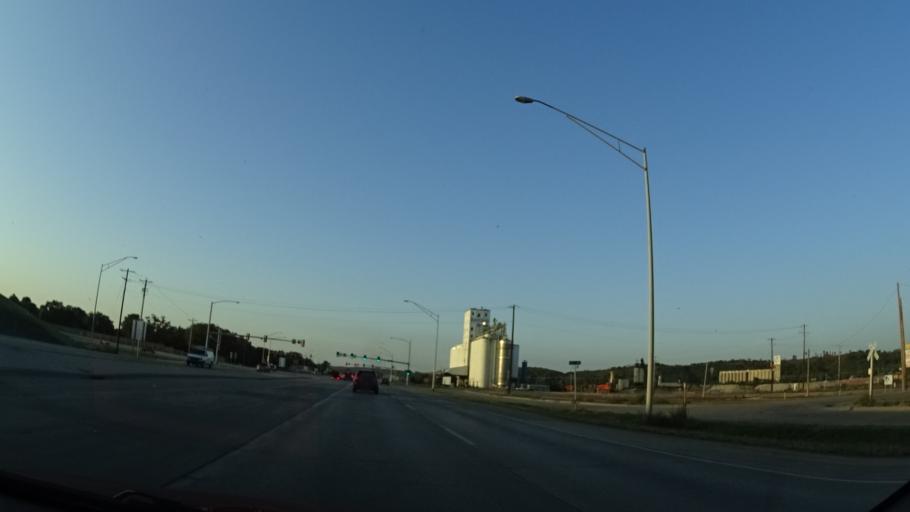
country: US
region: Iowa
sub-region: Pottawattamie County
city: Council Bluffs
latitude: 41.2323
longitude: -95.8513
